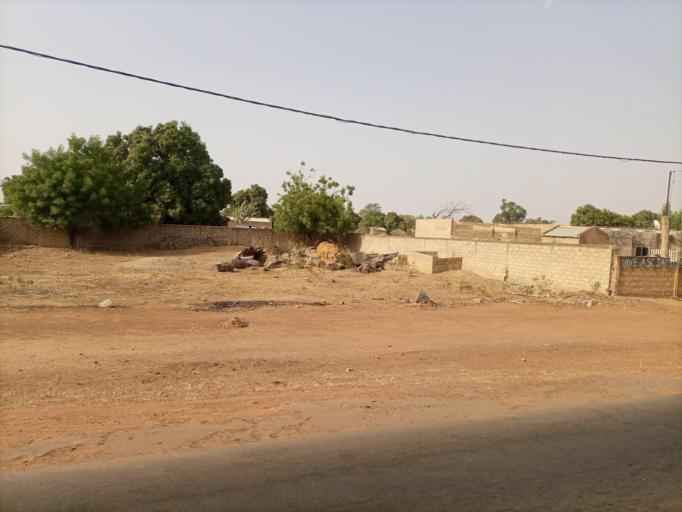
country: SN
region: Fatick
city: Foundiougne
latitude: 14.1216
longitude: -16.4326
